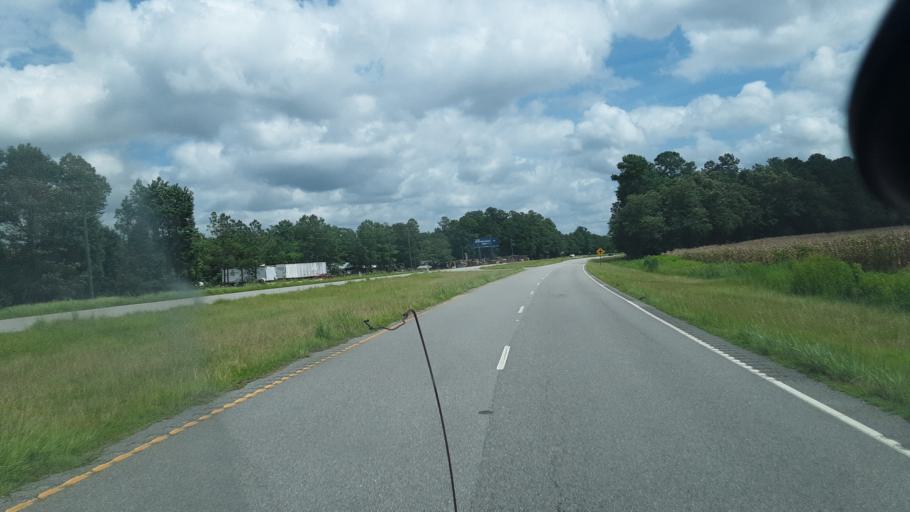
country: US
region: South Carolina
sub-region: Horry County
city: Loris
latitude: 34.1085
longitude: -78.9391
